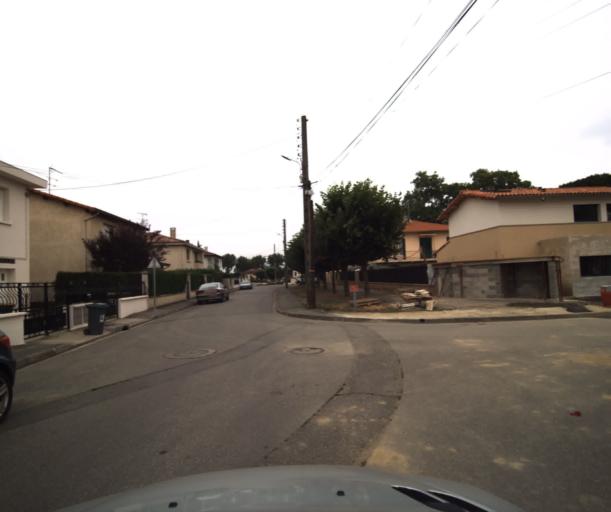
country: FR
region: Midi-Pyrenees
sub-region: Departement de la Haute-Garonne
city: Portet-sur-Garonne
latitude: 43.5258
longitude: 1.4073
